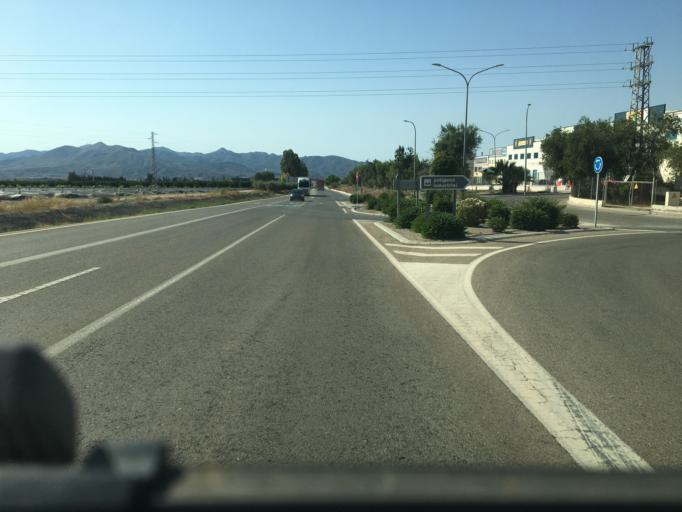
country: ES
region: Andalusia
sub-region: Provincia de Almeria
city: Huercal-Overa
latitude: 37.4160
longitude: -1.9662
